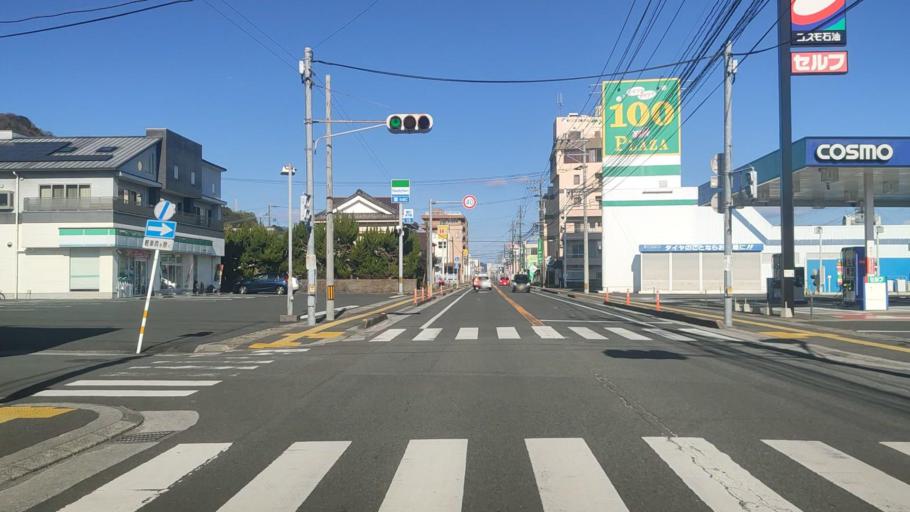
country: JP
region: Oita
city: Saiki
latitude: 32.9618
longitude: 131.9019
